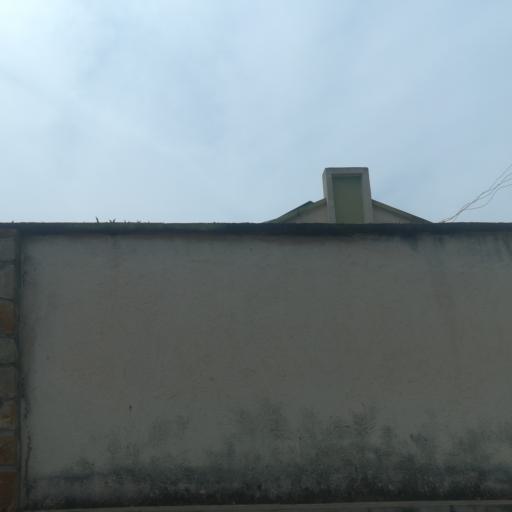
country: NG
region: Plateau
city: Jos
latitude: 9.8781
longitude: 8.8711
